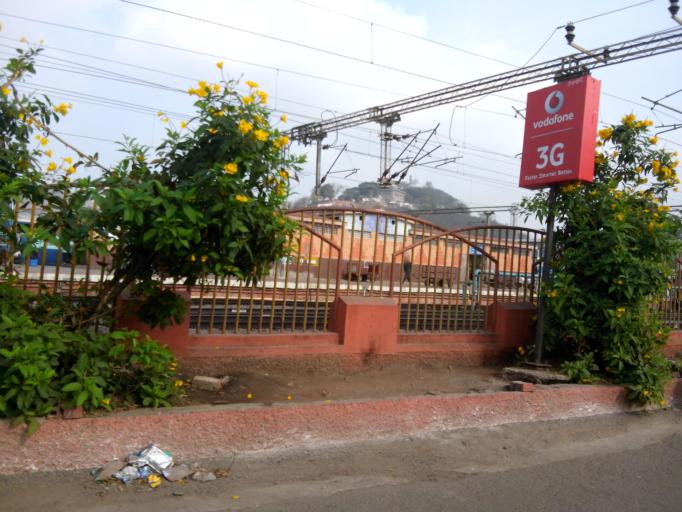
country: IN
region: Andhra Pradesh
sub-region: Krishna
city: Vijayawada
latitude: 16.5152
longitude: 80.6178
